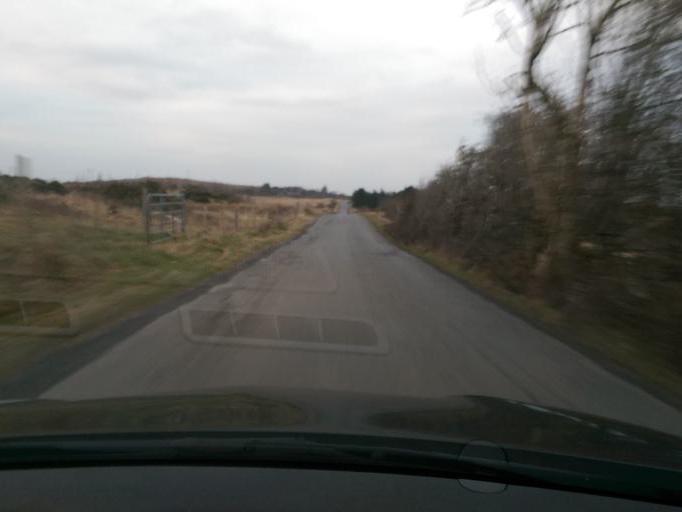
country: IE
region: Connaught
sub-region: County Galway
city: Bearna
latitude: 53.2860
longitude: -9.1634
